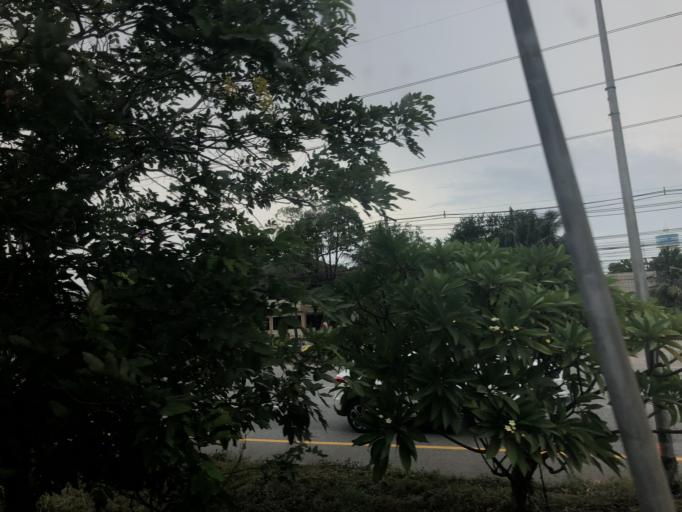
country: TH
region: Chon Buri
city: Bang Lamung
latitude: 13.0438
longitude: 100.9269
